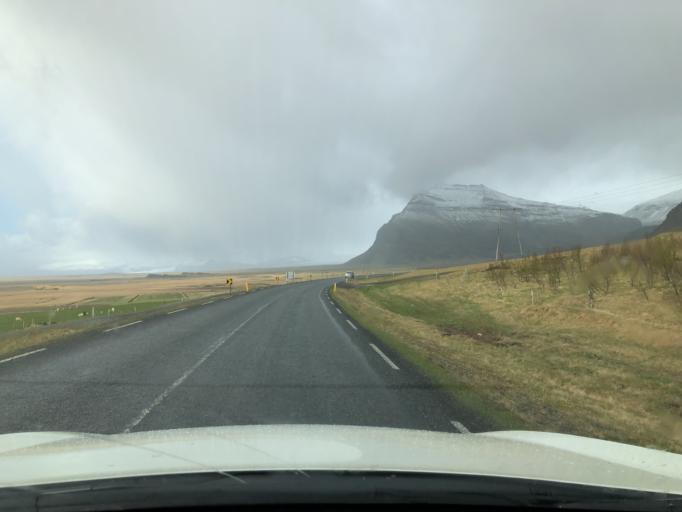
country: IS
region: East
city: Hoefn
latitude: 64.1296
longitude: -16.0249
